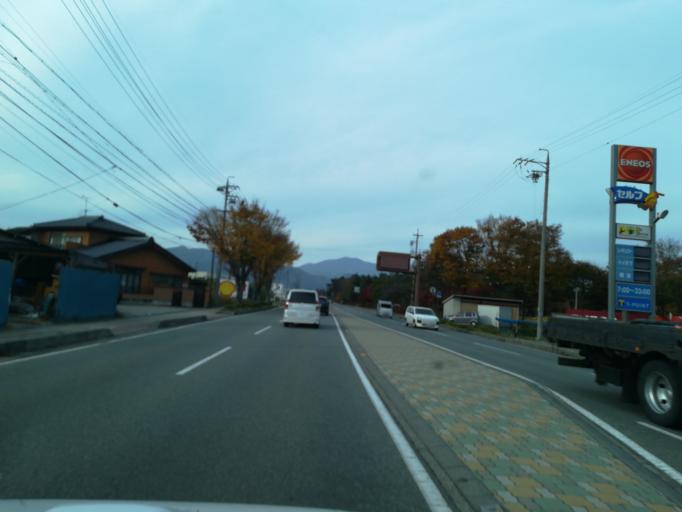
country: JP
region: Nagano
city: Nagano-shi
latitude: 36.5877
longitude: 138.1876
